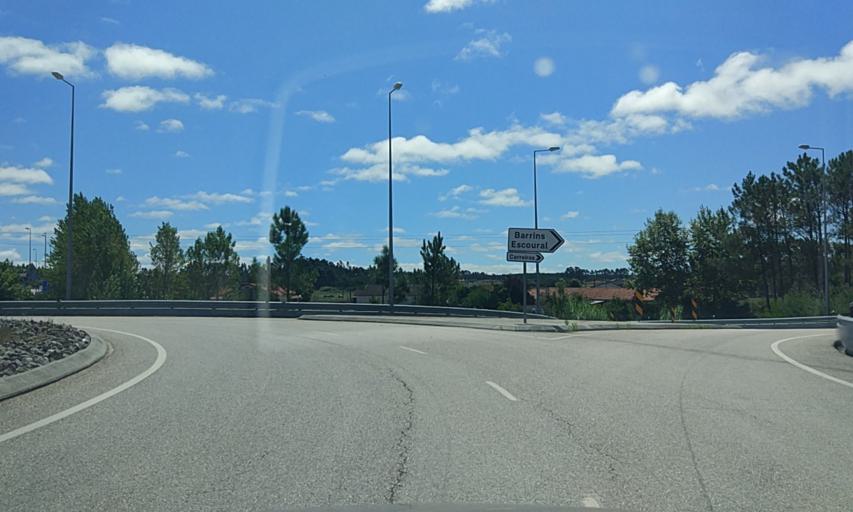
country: PT
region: Coimbra
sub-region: Montemor-O-Velho
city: Arazede
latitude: 40.3317
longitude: -8.7277
